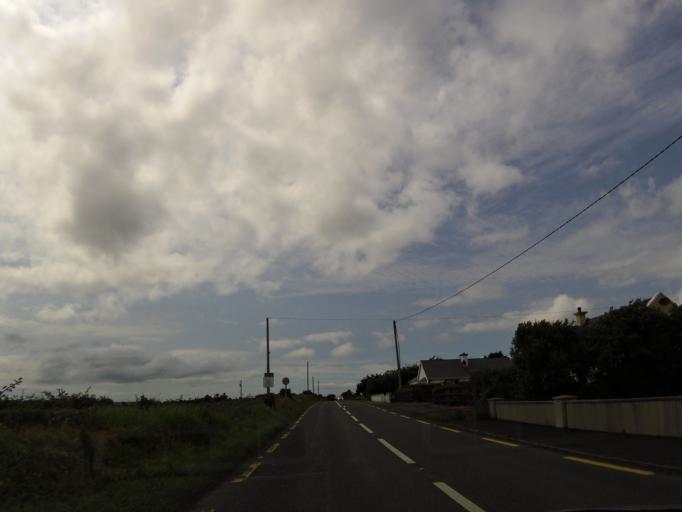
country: IE
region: Munster
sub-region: An Clar
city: Kilrush
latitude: 52.6725
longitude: -9.5663
